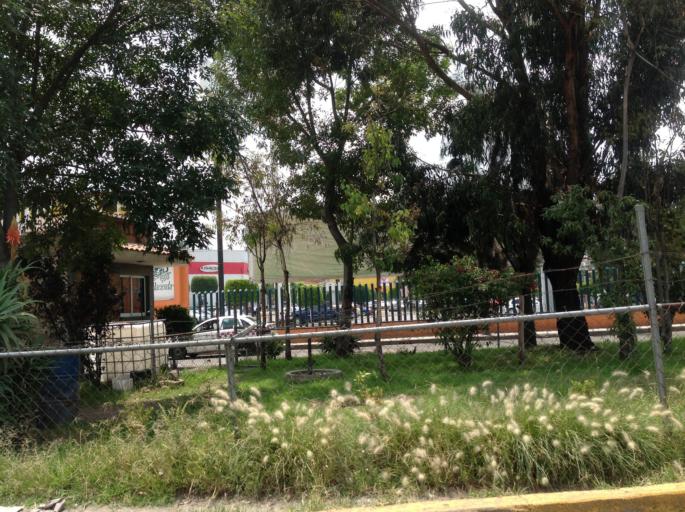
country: MX
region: Mexico
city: Ciudad Lopez Mateos
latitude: 19.6074
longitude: -99.2289
